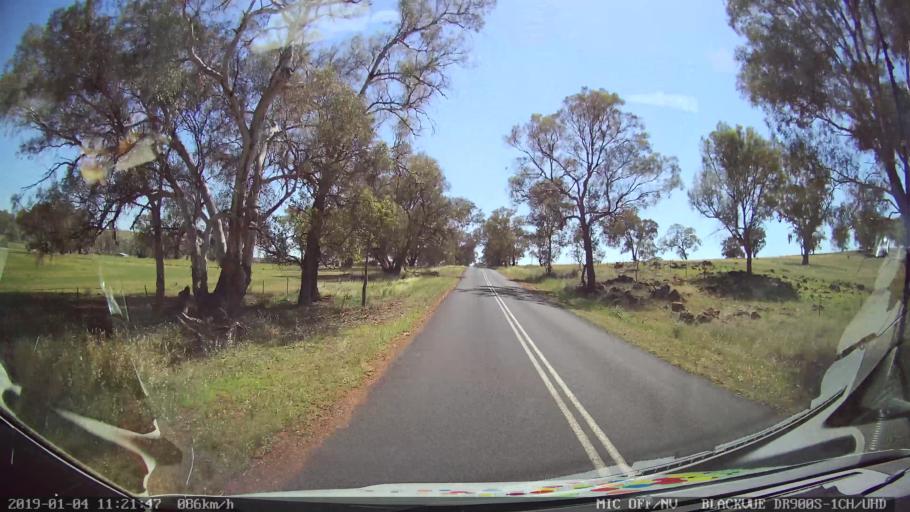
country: AU
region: New South Wales
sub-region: Cabonne
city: Molong
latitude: -33.1519
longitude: 148.7150
